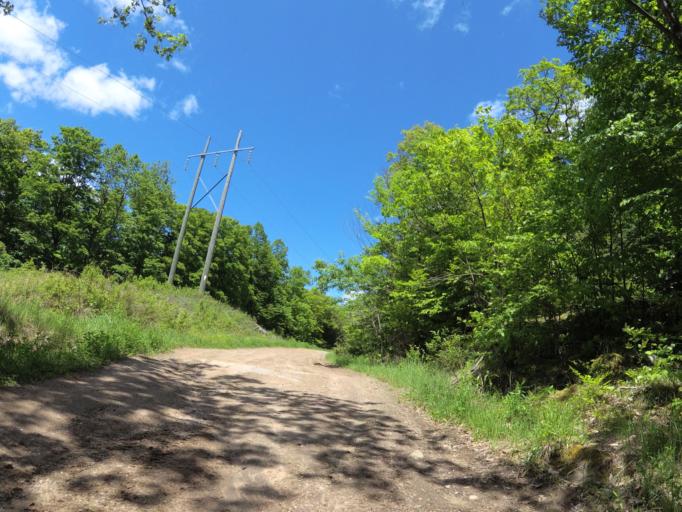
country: CA
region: Ontario
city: Renfrew
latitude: 45.0212
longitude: -76.8907
